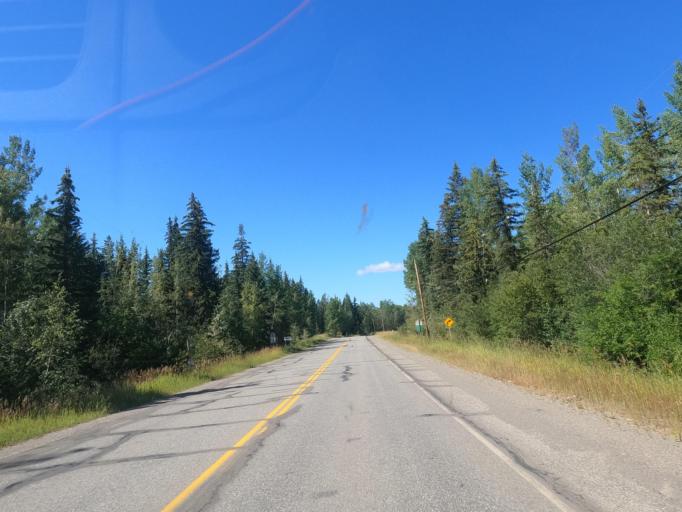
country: CA
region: British Columbia
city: Quesnel
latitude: 53.0202
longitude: -122.4588
